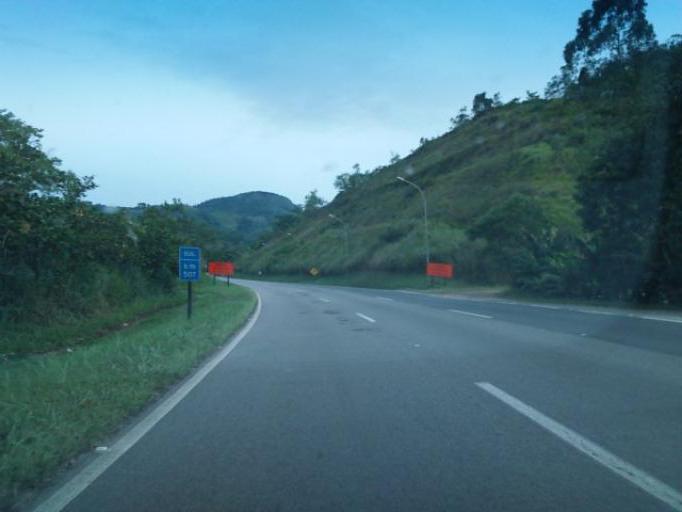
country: BR
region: Sao Paulo
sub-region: Cajati
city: Cajati
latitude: -24.8087
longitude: -48.2154
